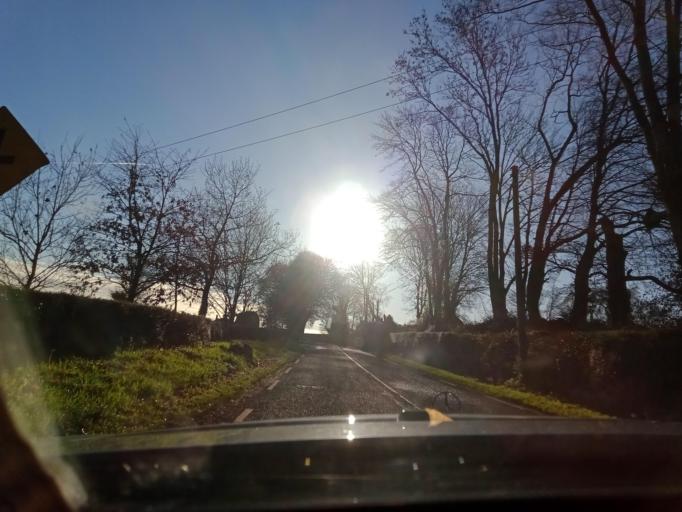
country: IE
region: Leinster
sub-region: Kilkenny
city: Piltown
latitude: 52.3755
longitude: -7.3399
